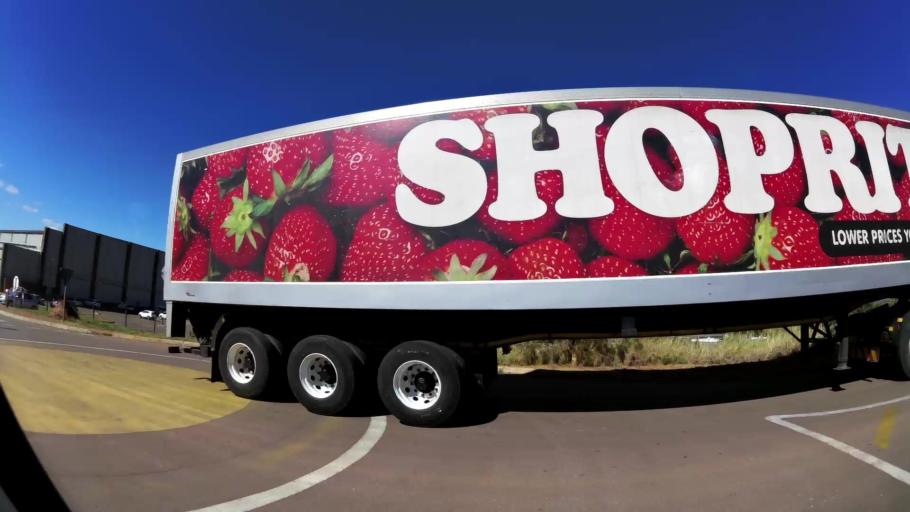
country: ZA
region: Limpopo
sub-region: Mopani District Municipality
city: Tzaneen
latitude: -23.8224
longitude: 30.1552
